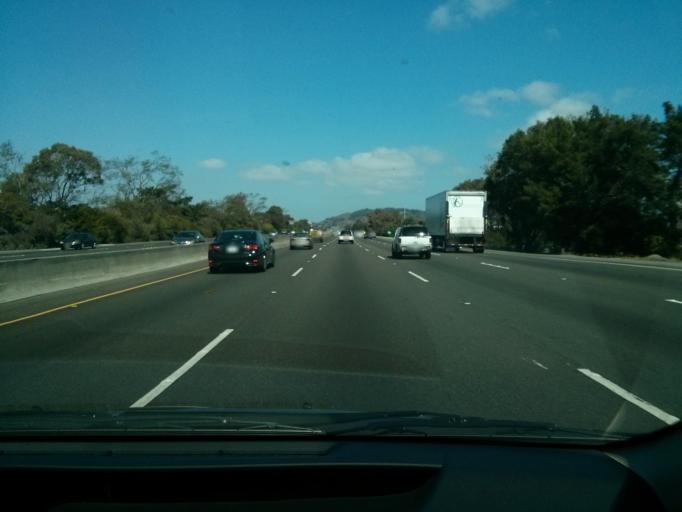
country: US
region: California
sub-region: San Mateo County
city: Brisbane
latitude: 37.6794
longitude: -122.3884
